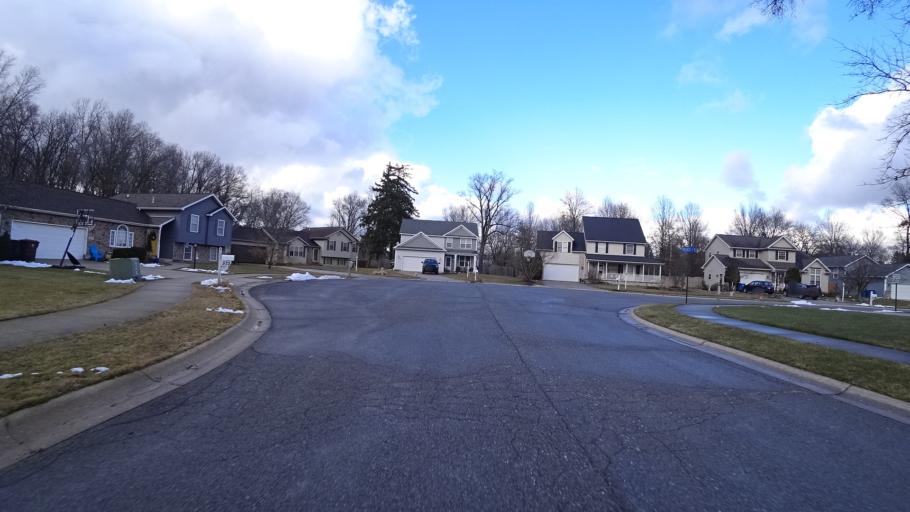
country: US
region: Indiana
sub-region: Porter County
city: Porter
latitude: 41.6071
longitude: -87.0861
